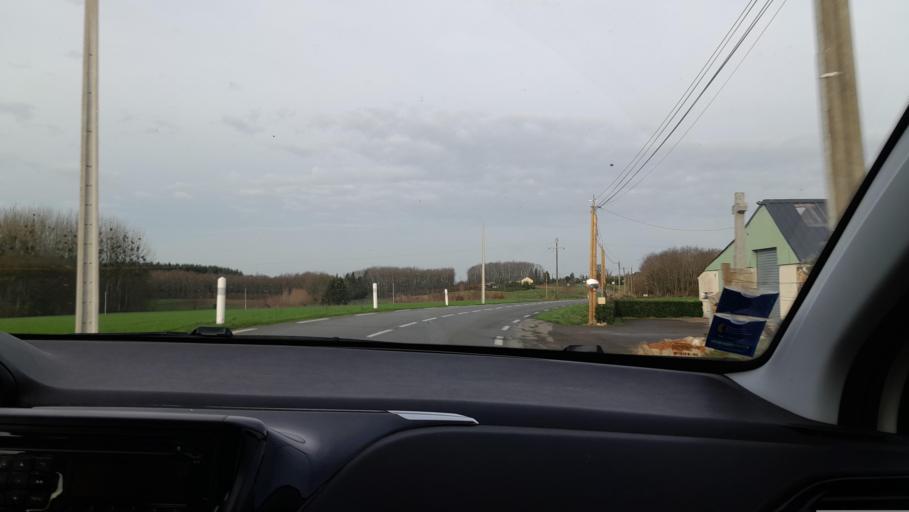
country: FR
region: Brittany
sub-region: Departement d'Ille-et-Vilaine
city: La Guerche-de-Bretagne
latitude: 47.9145
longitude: -1.2034
